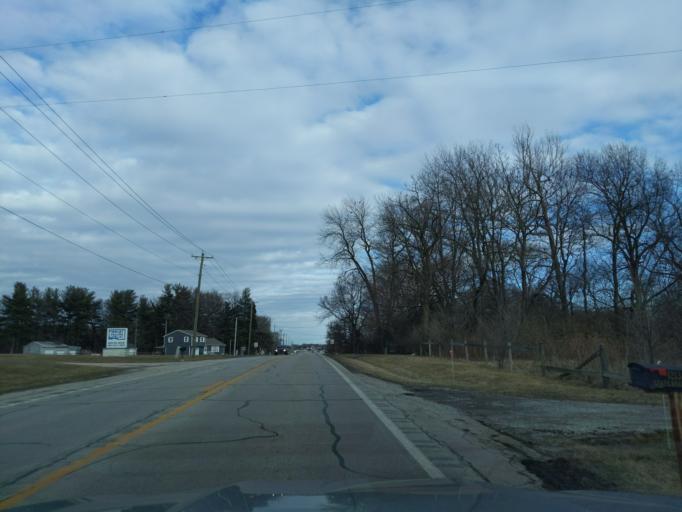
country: US
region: Indiana
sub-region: Tippecanoe County
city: Shadeland
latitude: 40.3836
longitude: -86.9278
